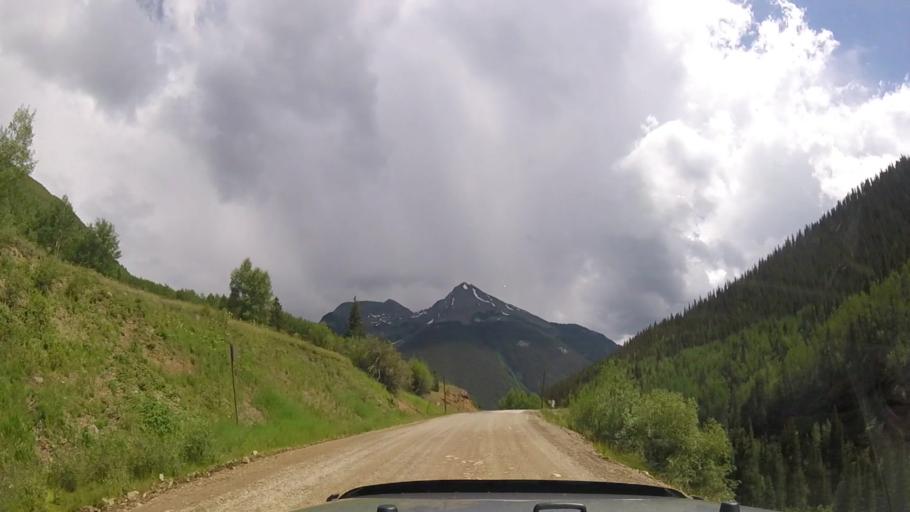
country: US
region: Colorado
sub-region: San Juan County
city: Silverton
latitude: 37.8238
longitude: -107.6659
